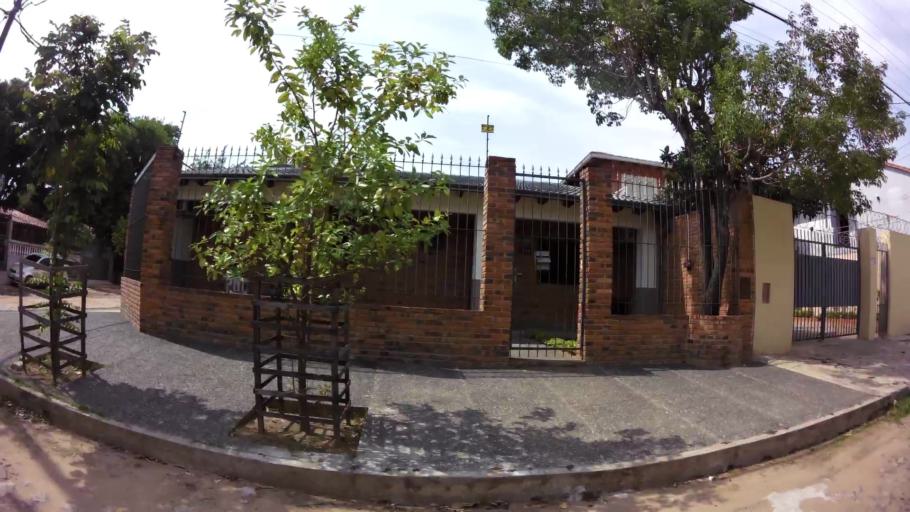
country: PY
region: Asuncion
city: Asuncion
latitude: -25.2603
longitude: -57.5857
